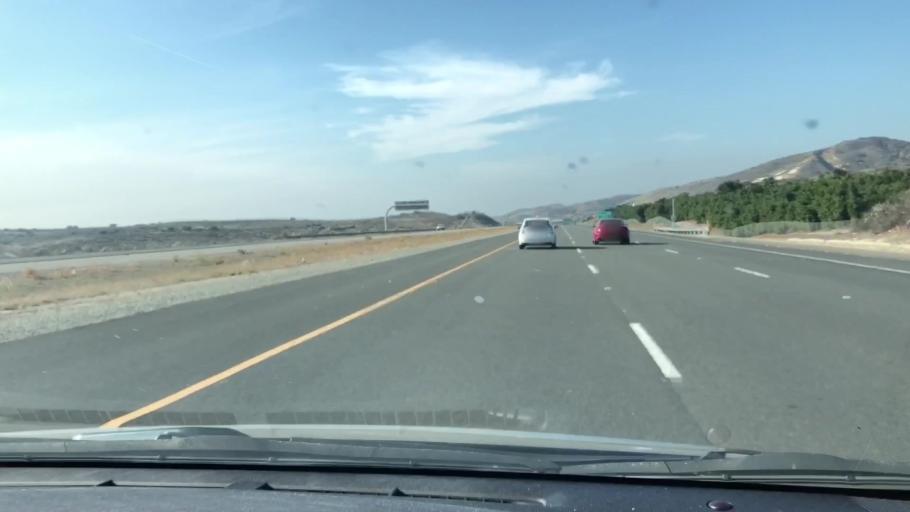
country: US
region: California
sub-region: Orange County
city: Foothill Ranch
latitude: 33.6877
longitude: -117.6807
